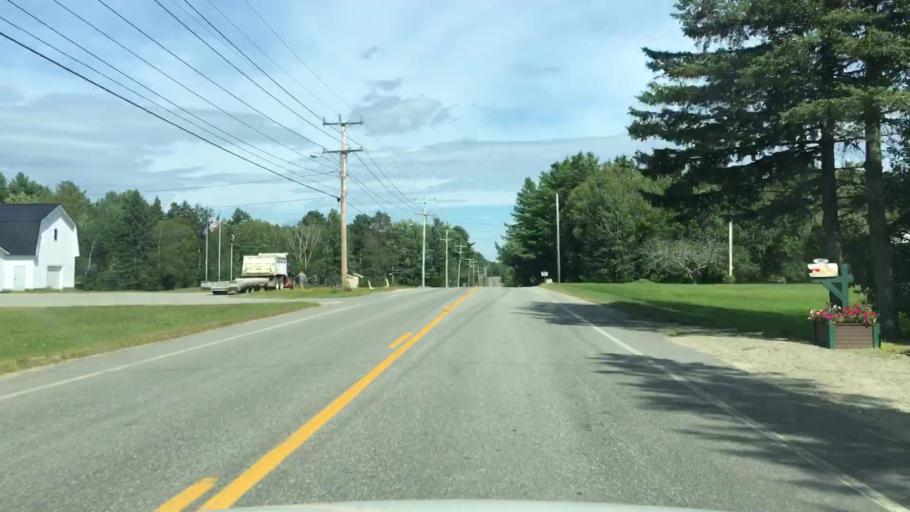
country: US
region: Maine
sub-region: Penobscot County
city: Lincoln
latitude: 45.4289
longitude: -68.4739
